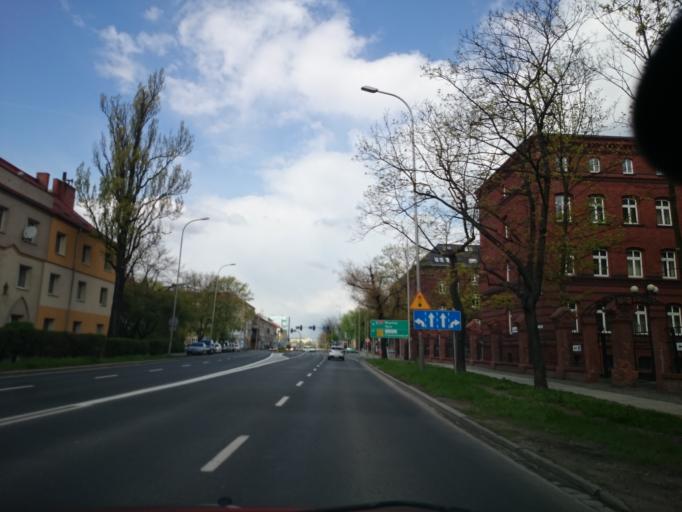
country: PL
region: Opole Voivodeship
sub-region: Powiat opolski
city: Opole
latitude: 50.6669
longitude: 17.9422
